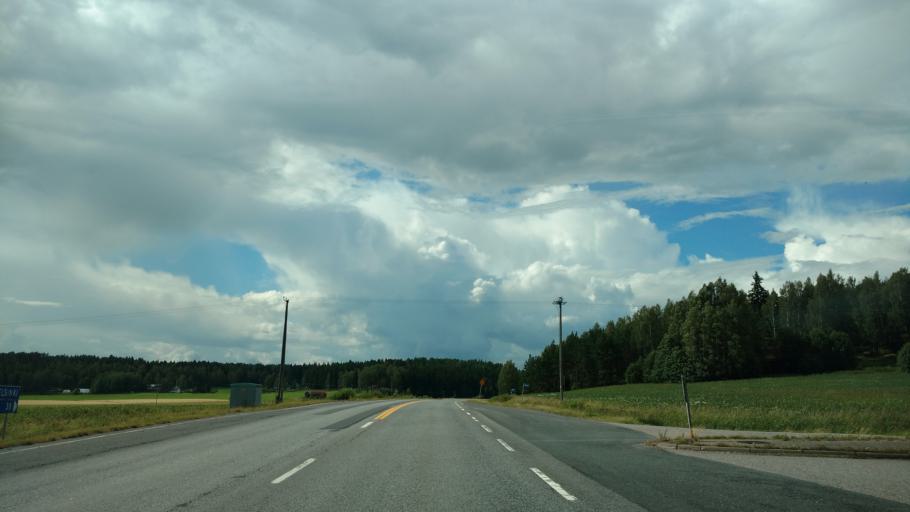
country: FI
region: Varsinais-Suomi
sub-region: Salo
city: Halikko
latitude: 60.3828
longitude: 22.8936
